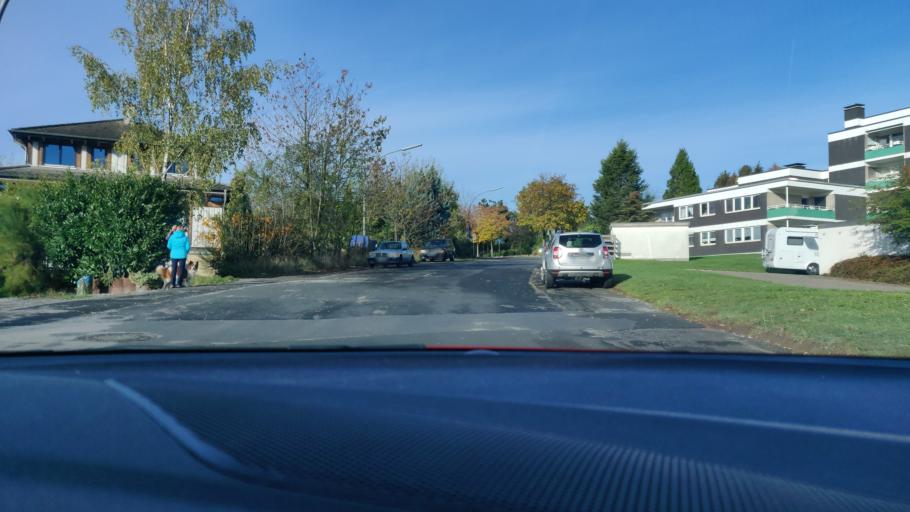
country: DE
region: North Rhine-Westphalia
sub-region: Regierungsbezirk Dusseldorf
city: Velbert
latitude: 51.3459
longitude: 7.0111
